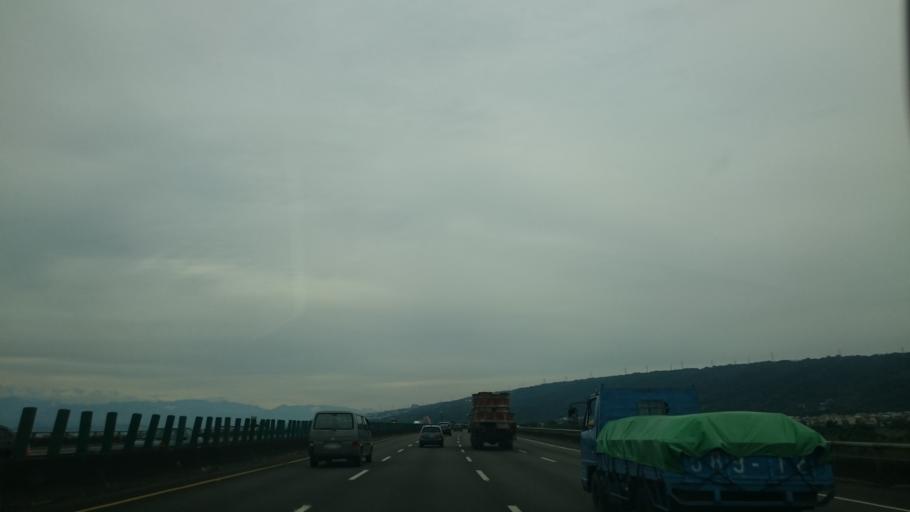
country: TW
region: Taiwan
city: Zhongxing New Village
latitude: 23.9852
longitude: 120.6528
